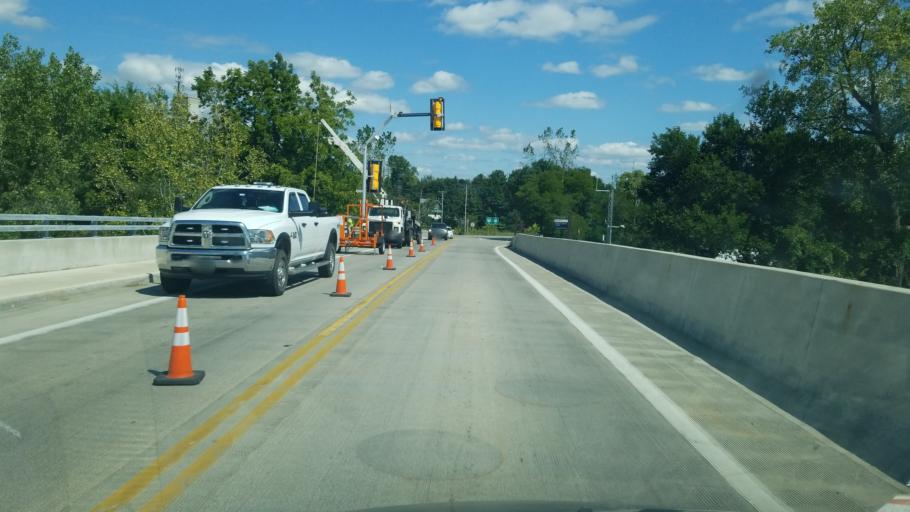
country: US
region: Ohio
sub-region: Wood County
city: Weston
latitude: 41.4147
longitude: -83.8606
